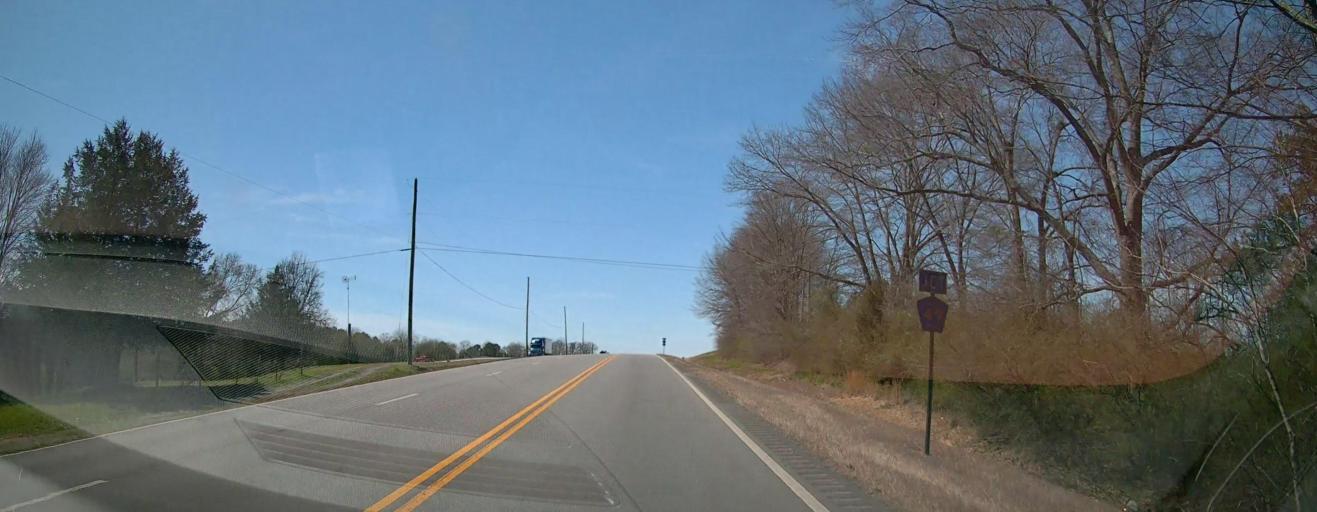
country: US
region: Alabama
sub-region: Blount County
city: Blountsville
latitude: 34.1737
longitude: -86.5544
